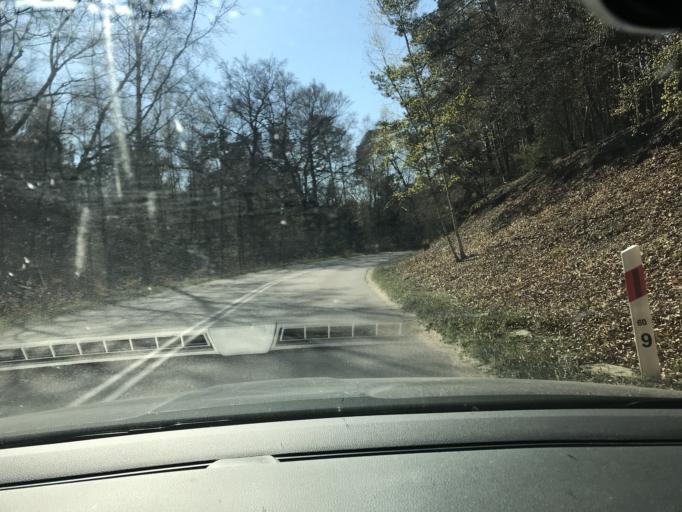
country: PL
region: Pomeranian Voivodeship
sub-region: Powiat nowodworski
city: Krynica Morska
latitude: 54.3643
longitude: 19.3682
